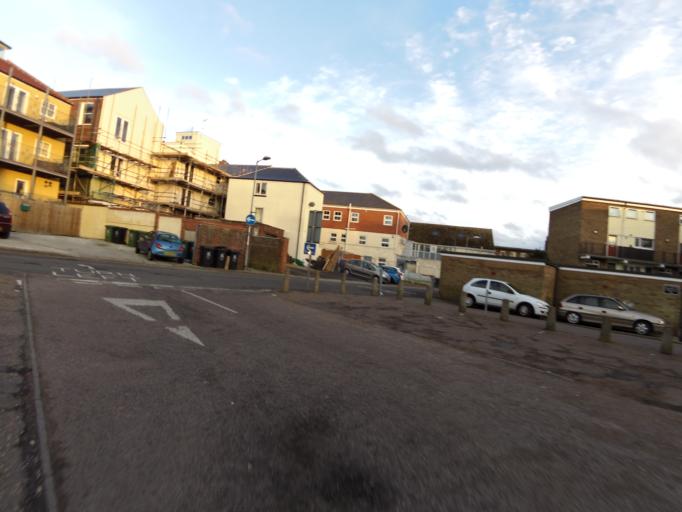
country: GB
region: England
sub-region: Norfolk
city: Great Yarmouth
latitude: 52.6053
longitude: 1.7279
